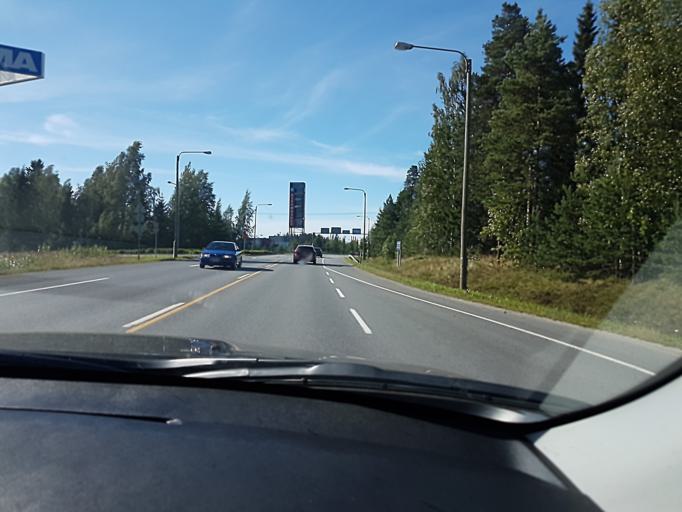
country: FI
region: Southern Ostrobothnia
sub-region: Seinaejoki
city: Nurmo
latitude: 62.7926
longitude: 22.8816
